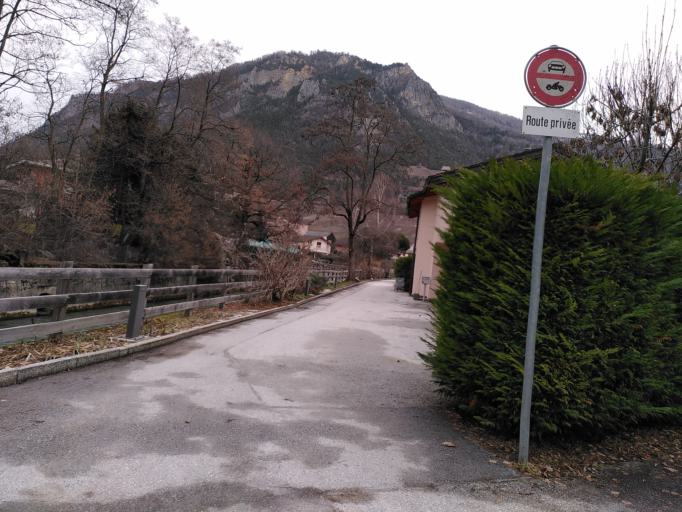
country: CH
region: Valais
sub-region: Herens District
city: Vex
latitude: 46.2303
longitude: 7.3993
